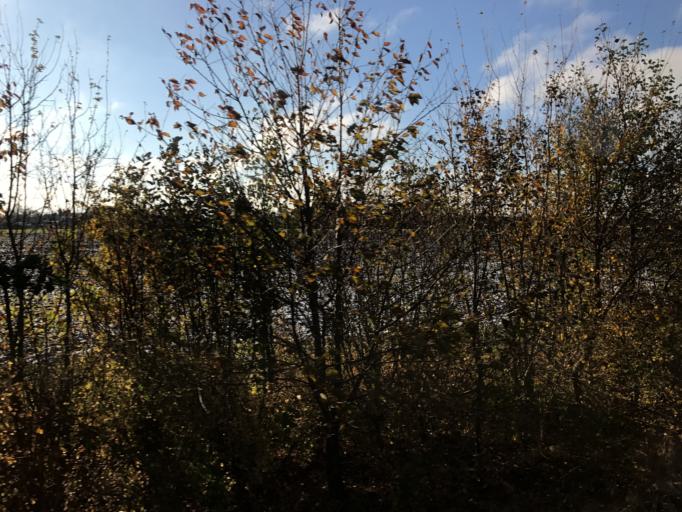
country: DK
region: Zealand
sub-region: Stevns Kommune
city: Harlev
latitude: 55.3560
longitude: 12.2375
